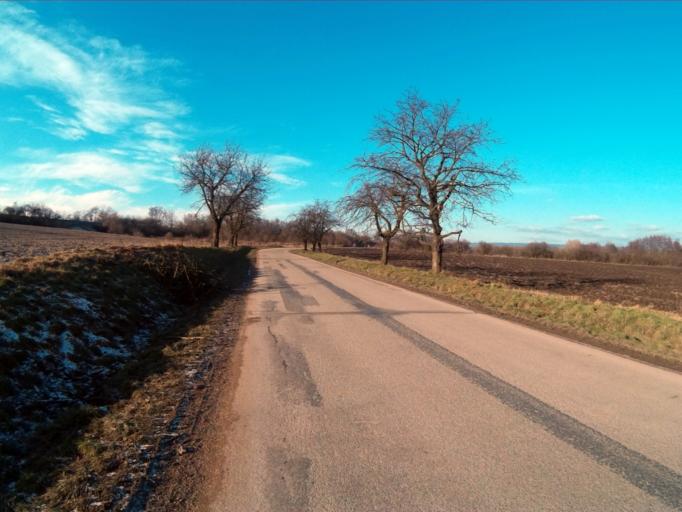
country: CZ
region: South Moravian
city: Krenovice
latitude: 49.1525
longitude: 16.8219
